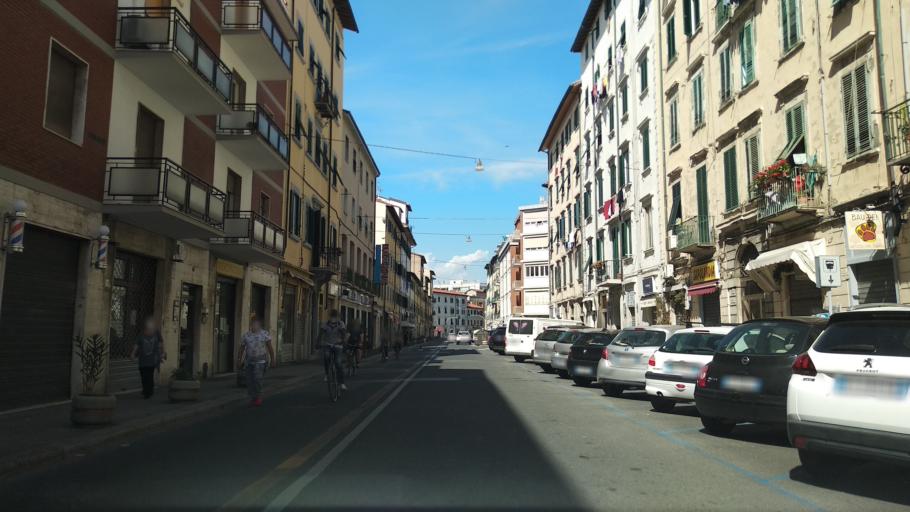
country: IT
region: Tuscany
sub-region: Provincia di Livorno
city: Livorno
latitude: 43.5549
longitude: 10.3154
